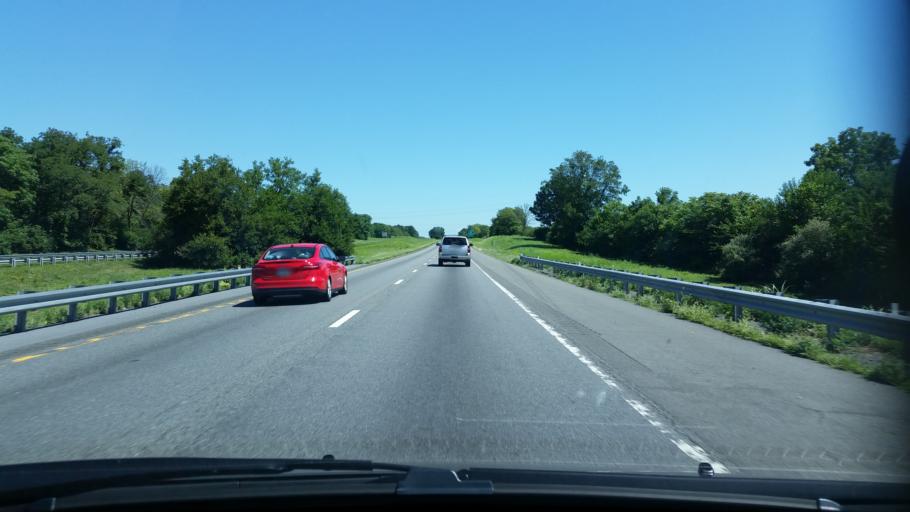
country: US
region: West Virginia
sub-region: Berkeley County
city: Inwood
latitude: 39.2688
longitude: -78.0949
